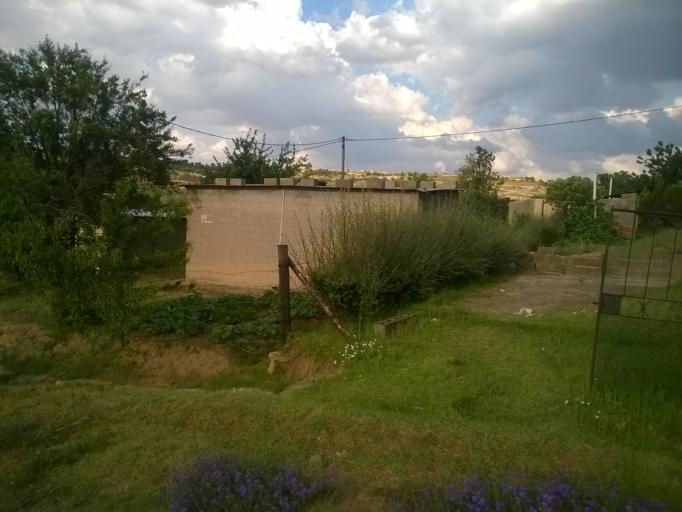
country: LS
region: Berea
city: Teyateyaneng
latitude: -29.1462
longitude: 27.7298
